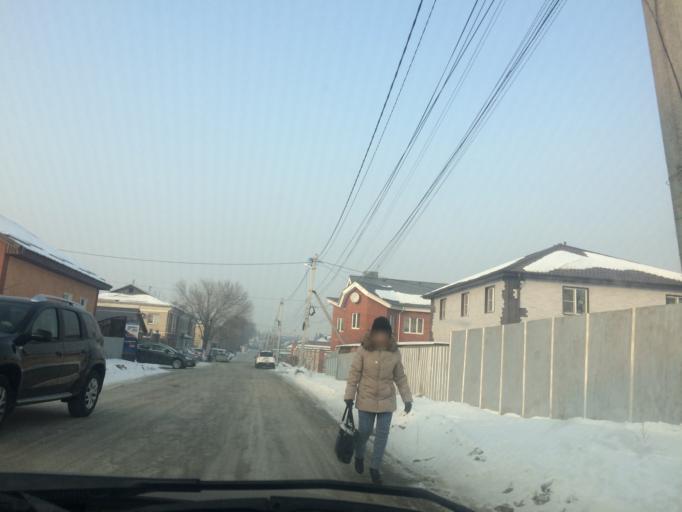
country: RU
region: Chelyabinsk
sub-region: Gorod Magnitogorsk
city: Magnitogorsk
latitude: 53.4188
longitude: 58.9641
